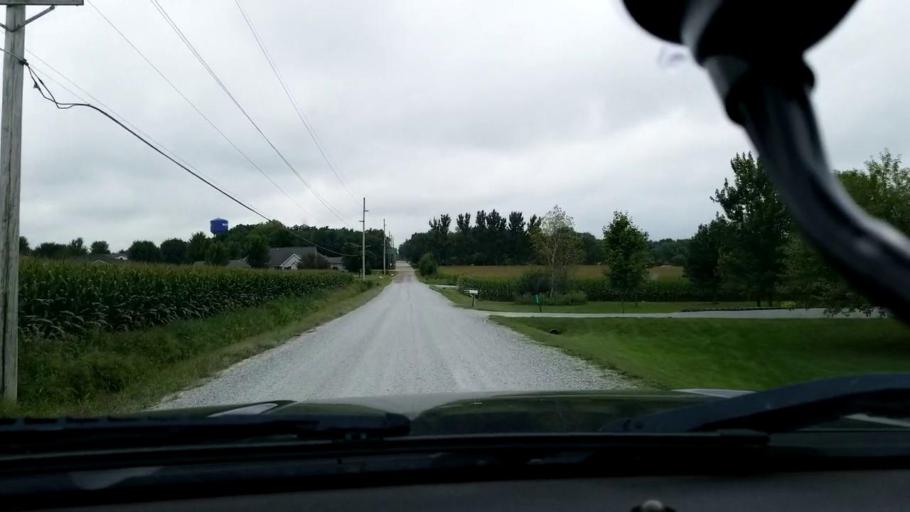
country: US
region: Iowa
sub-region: Buchanan County
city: Independence
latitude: 42.4861
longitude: -91.8846
